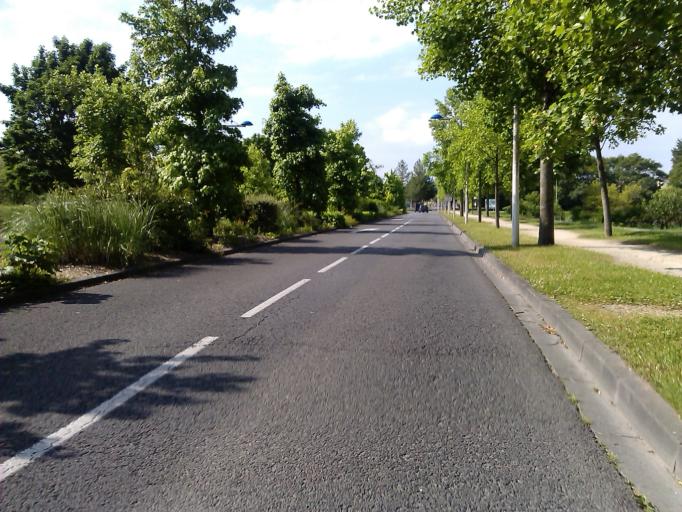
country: FR
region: Poitou-Charentes
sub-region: Departement de la Charente
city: Angouleme
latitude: 45.6551
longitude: 0.1396
